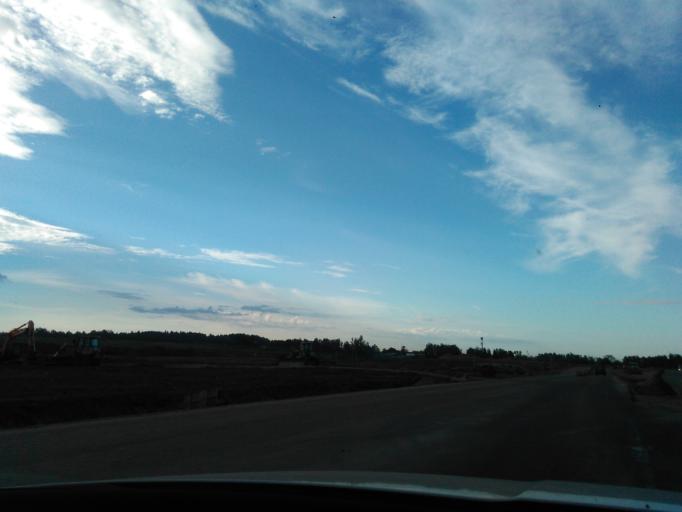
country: RU
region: Moskovskaya
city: Sheremet'yevskiy
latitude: 55.9796
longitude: 37.4535
